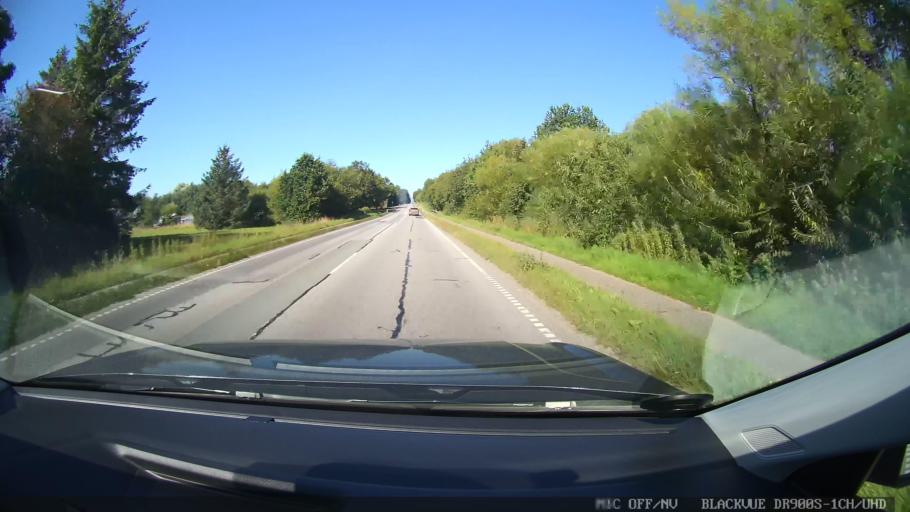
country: DK
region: Central Jutland
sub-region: Randers Kommune
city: Spentrup
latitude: 56.4998
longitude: 10.0238
